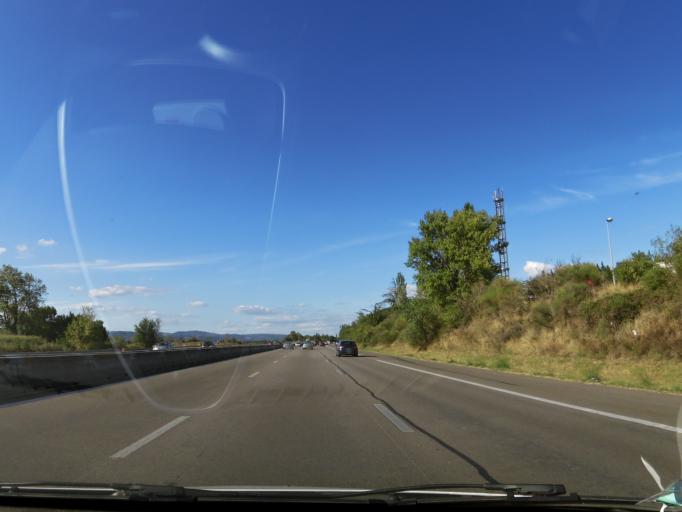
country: FR
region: Rhone-Alpes
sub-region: Departement de la Drome
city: Saulce-sur-Rhone
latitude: 44.7221
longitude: 4.7862
